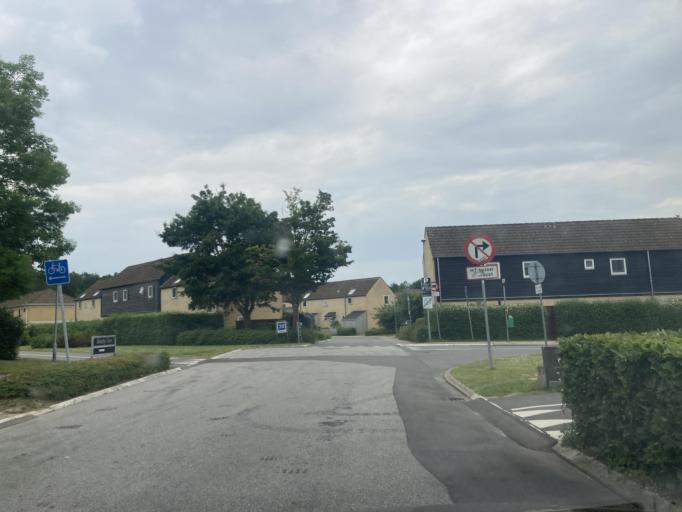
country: DK
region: Capital Region
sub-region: Hoje-Taastrup Kommune
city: Taastrup
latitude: 55.6394
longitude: 12.2778
